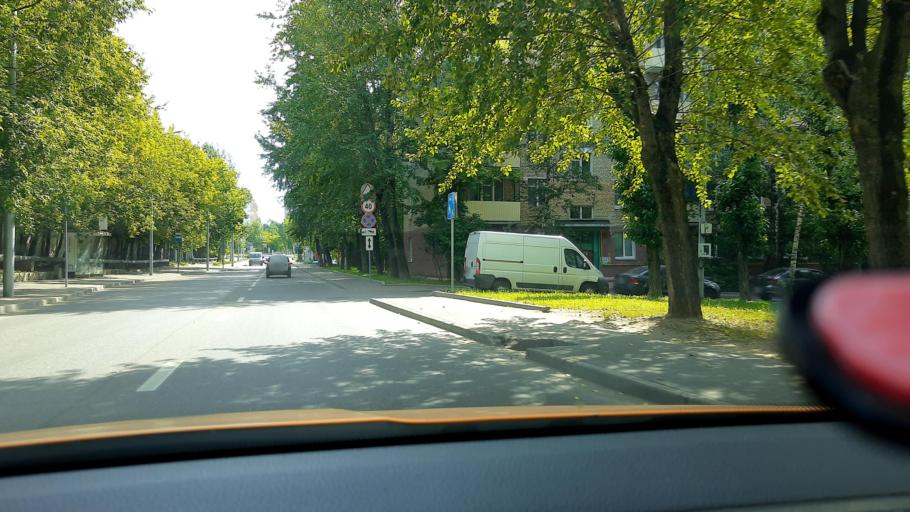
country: RU
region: Moskovskaya
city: Marfino
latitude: 55.7236
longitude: 37.3865
